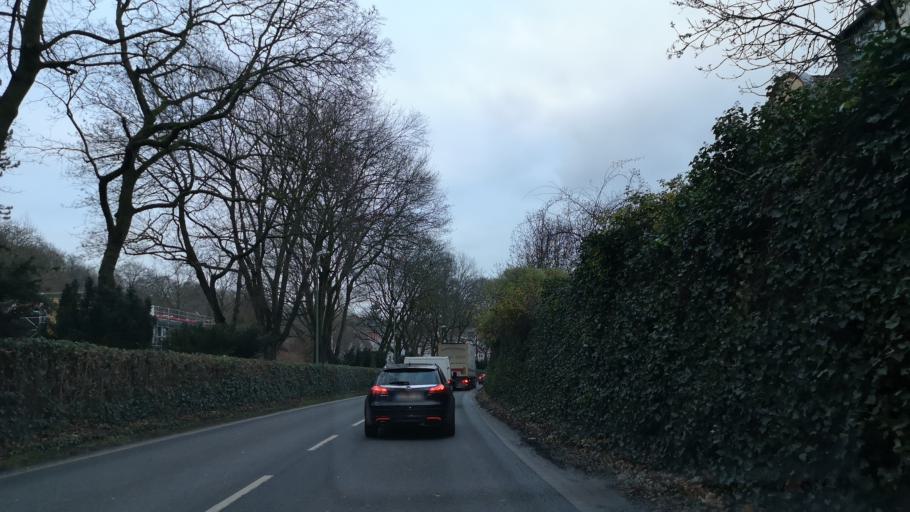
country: DE
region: North Rhine-Westphalia
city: Wetter (Ruhr)
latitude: 51.3476
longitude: 7.4192
